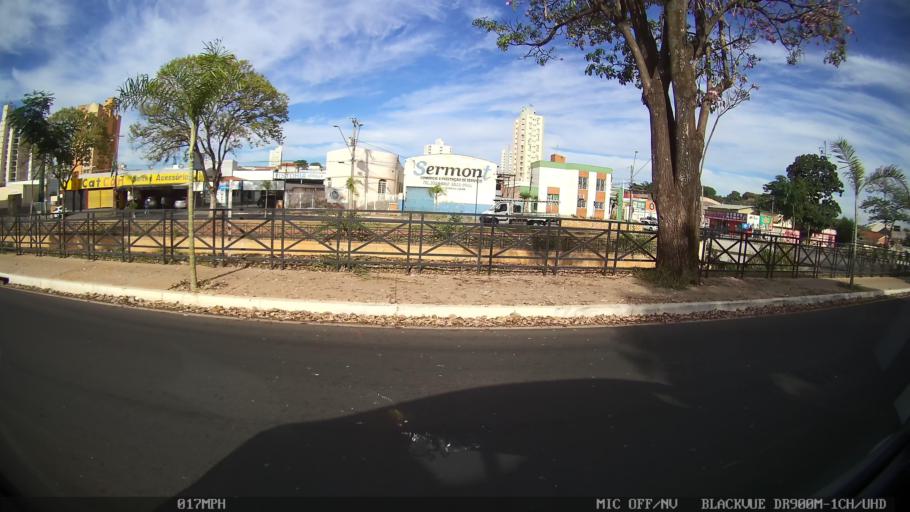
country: BR
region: Sao Paulo
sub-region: Catanduva
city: Catanduva
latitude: -21.1310
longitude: -48.9773
